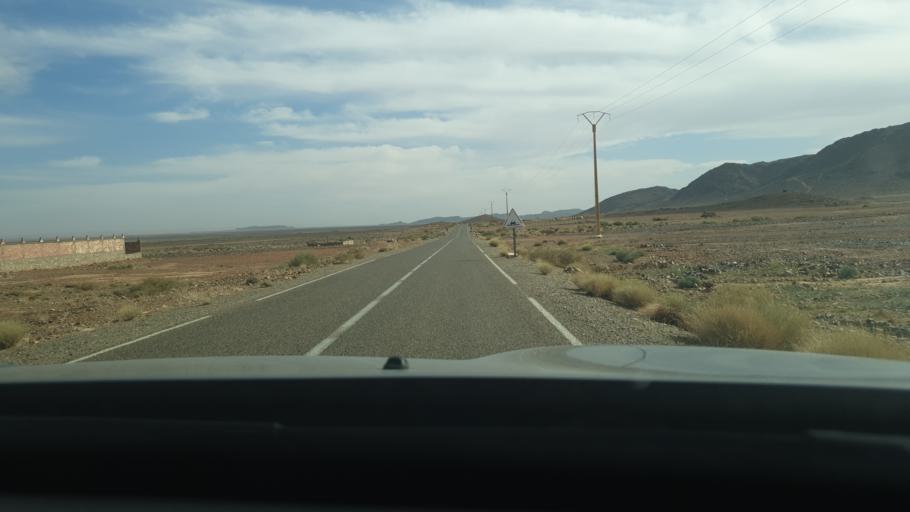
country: MA
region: Meknes-Tafilalet
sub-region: Errachidia
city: Fezna
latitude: 31.5281
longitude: -4.6348
